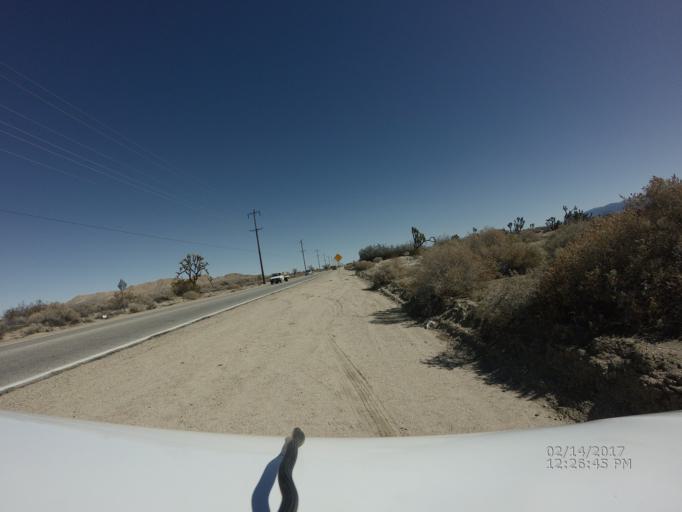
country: US
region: California
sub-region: Los Angeles County
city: Lake Los Angeles
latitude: 34.5800
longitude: -117.8884
